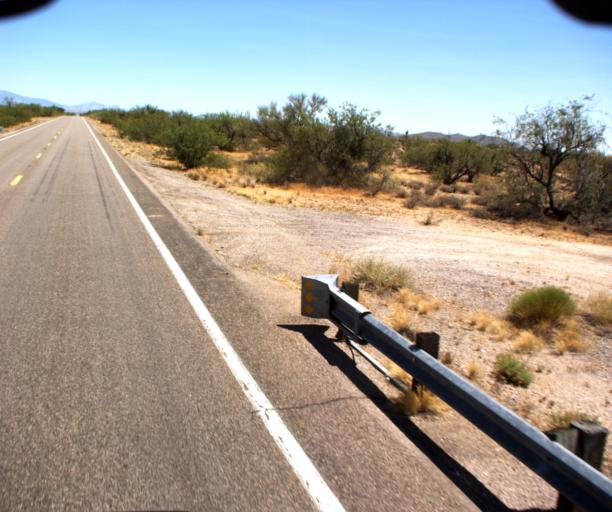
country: US
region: Arizona
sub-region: Pima County
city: Catalina
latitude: 32.7405
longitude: -111.1241
